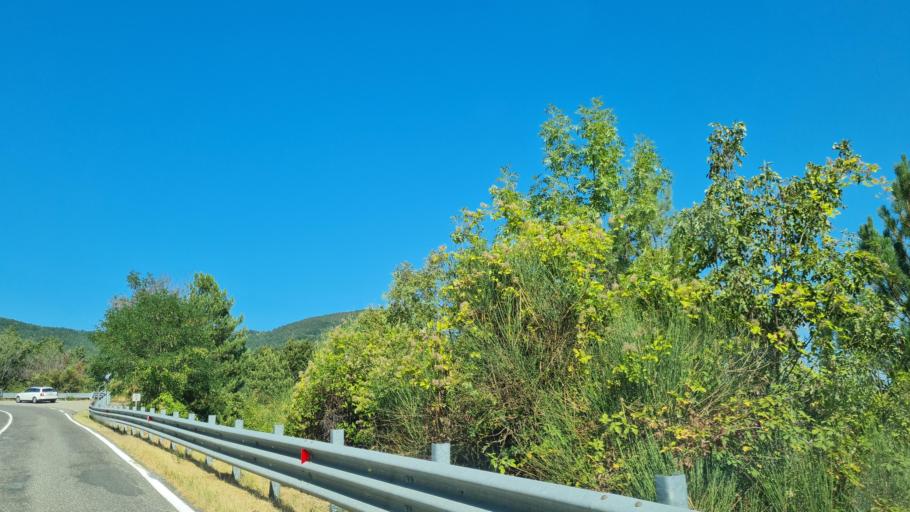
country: IT
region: Tuscany
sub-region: Provincia di Siena
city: Abbadia San Salvatore
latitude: 42.9211
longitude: 11.6963
